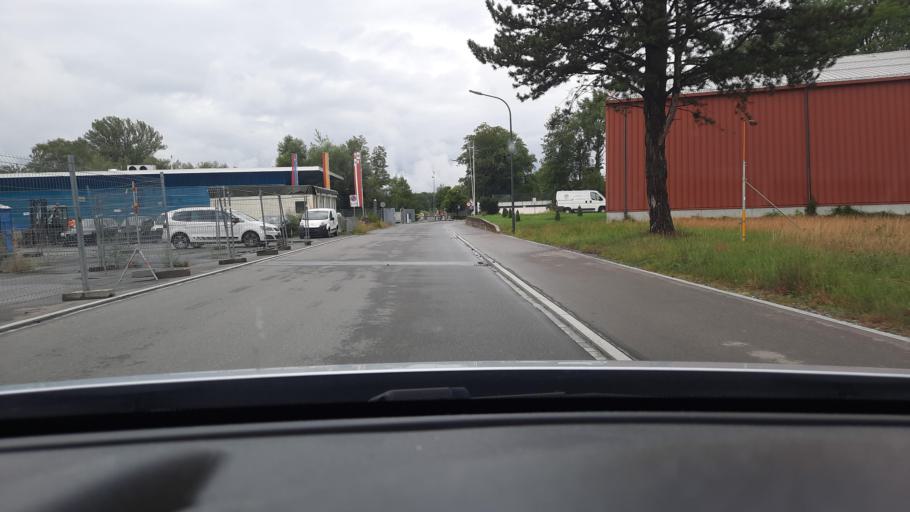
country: LI
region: Schaan
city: Schaan
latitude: 47.1504
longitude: 9.5072
